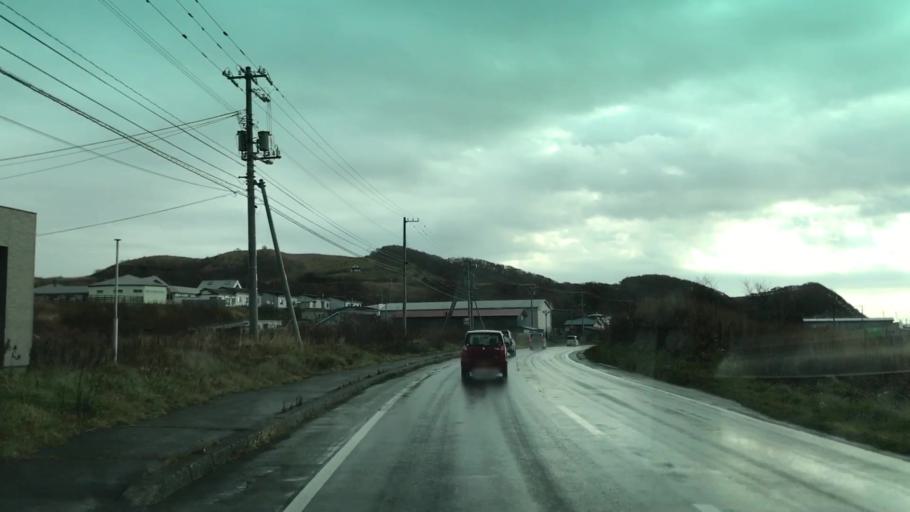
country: JP
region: Hokkaido
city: Shizunai-furukawacho
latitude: 42.1912
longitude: 142.6945
